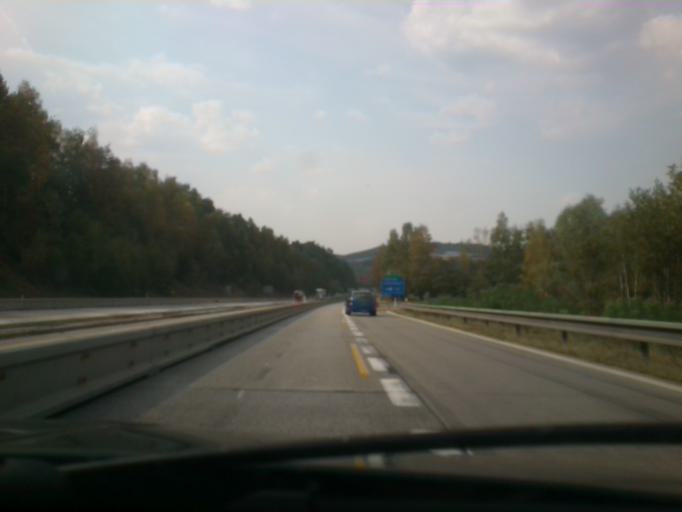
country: CZ
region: Central Bohemia
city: Ondrejov
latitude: 49.8621
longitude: 14.7890
